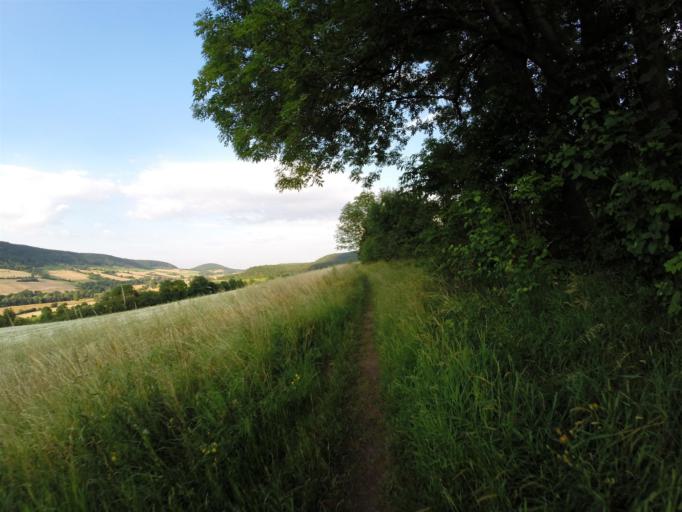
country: DE
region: Thuringia
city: Jena
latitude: 50.9277
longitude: 11.6359
